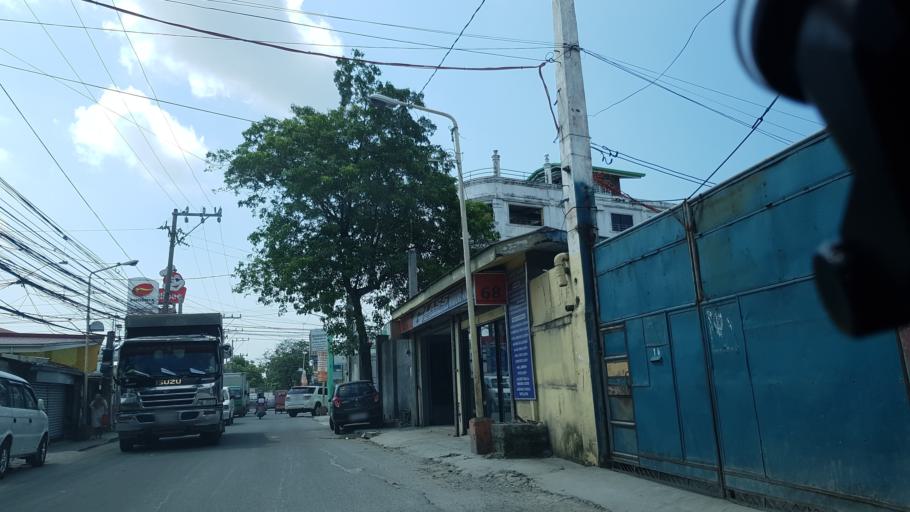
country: PH
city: Sambayanihan People's Village
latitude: 14.4626
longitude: 120.9903
